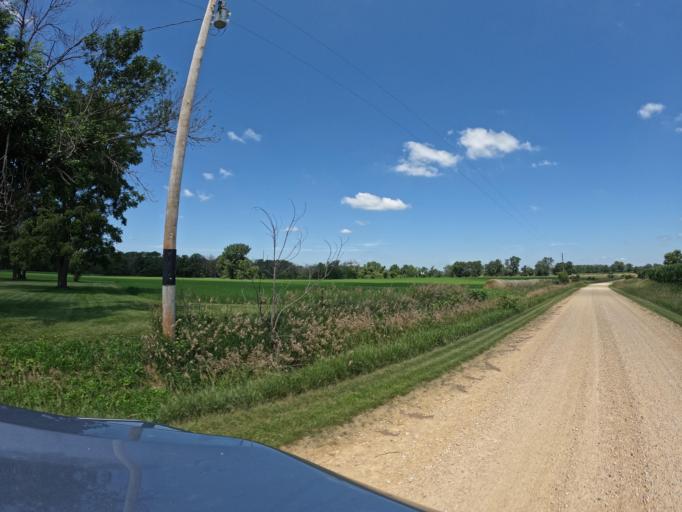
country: US
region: Iowa
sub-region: Clinton County
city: De Witt
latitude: 41.7747
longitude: -90.4297
